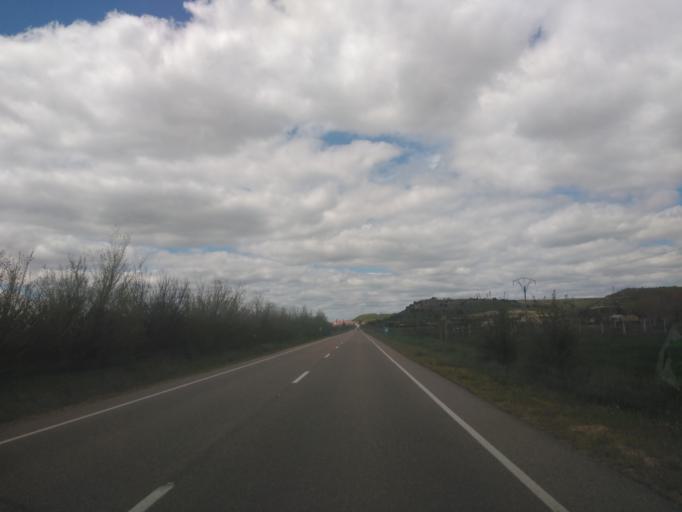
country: ES
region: Castille and Leon
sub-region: Provincia de Salamanca
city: Almenara de Tormes
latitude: 41.0560
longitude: -5.8002
